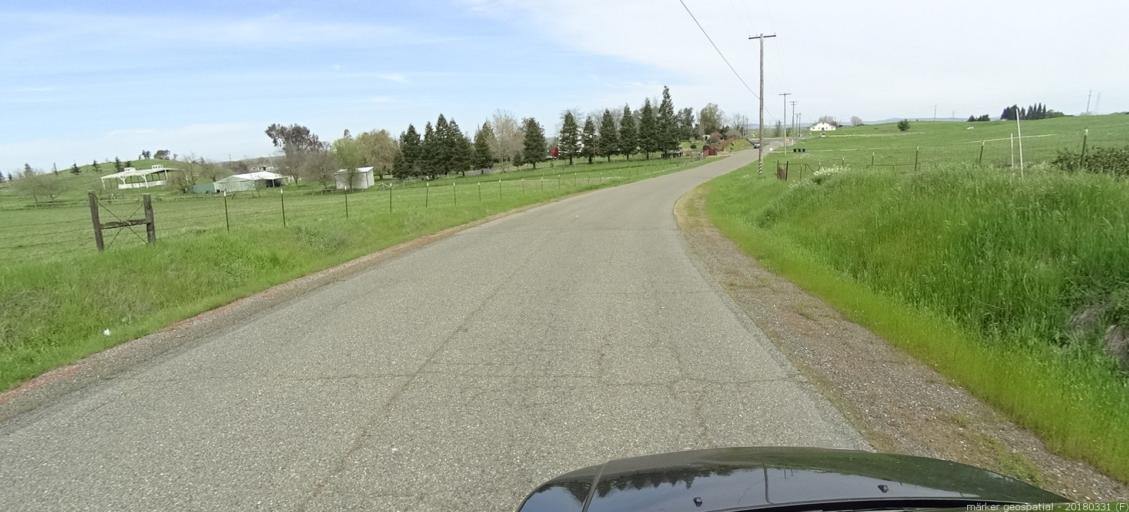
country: US
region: California
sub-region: Sacramento County
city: Rancho Murieta
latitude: 38.4930
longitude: -121.1477
